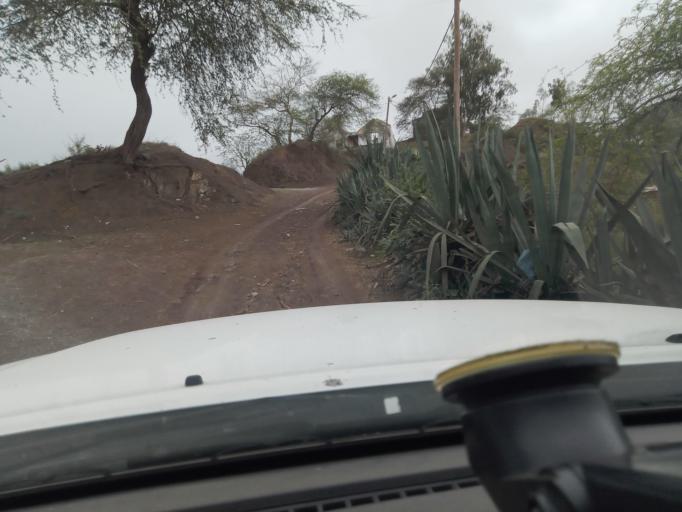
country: CV
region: Santa Catarina
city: Assomada
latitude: 15.1379
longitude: -23.6456
